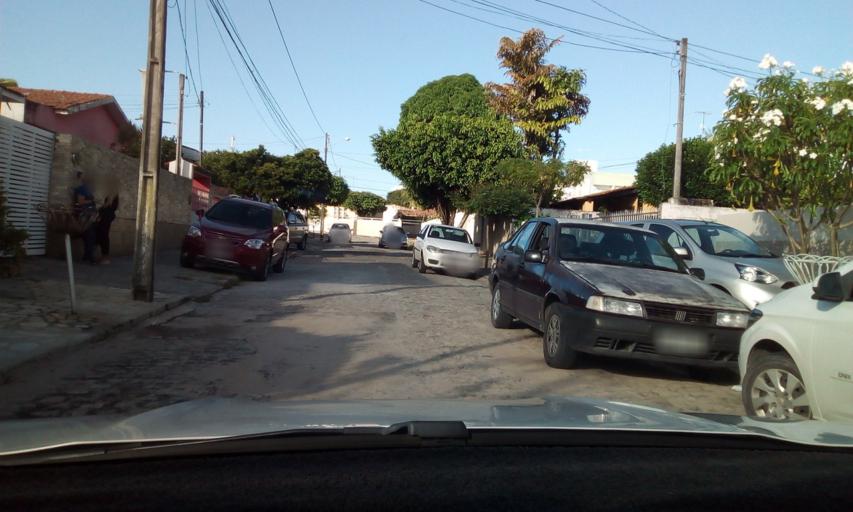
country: BR
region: Paraiba
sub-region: Joao Pessoa
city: Joao Pessoa
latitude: -7.1370
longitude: -34.8297
